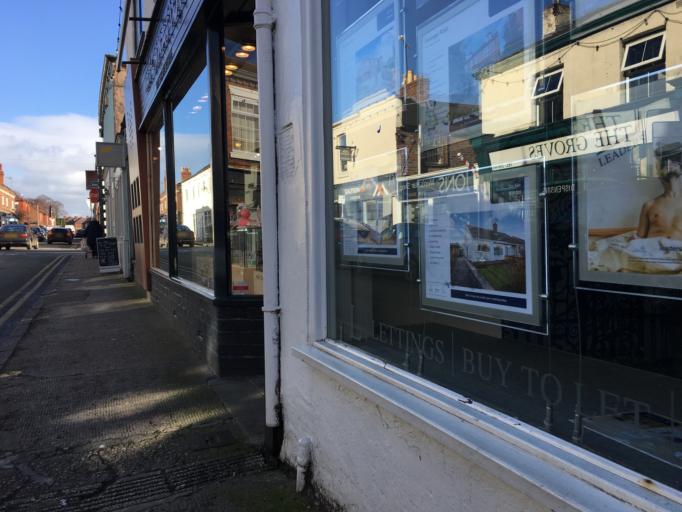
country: GB
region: England
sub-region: Cheshire West and Chester
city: Hoole
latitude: 53.1991
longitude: -2.8753
